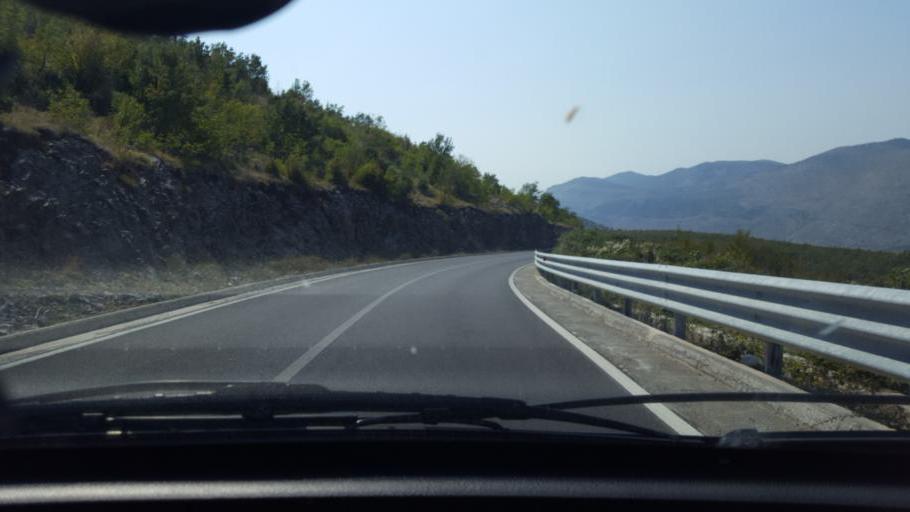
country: AL
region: Shkoder
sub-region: Rrethi i Malesia e Madhe
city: Kastrat
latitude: 42.3716
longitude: 19.4755
